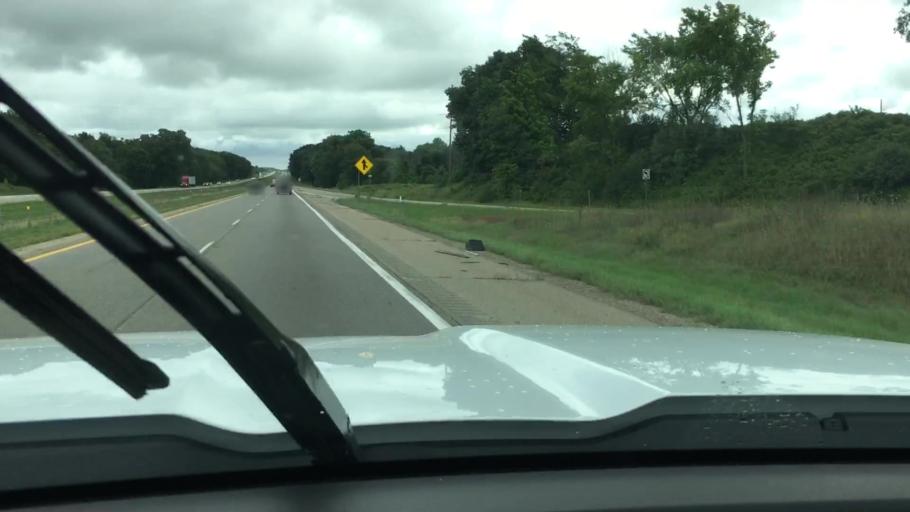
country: US
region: Michigan
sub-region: Ionia County
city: Ionia
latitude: 42.8800
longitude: -85.0718
